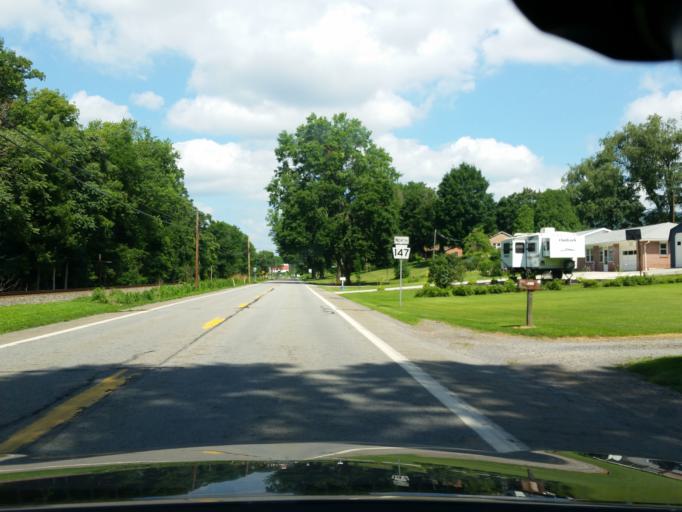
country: US
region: Pennsylvania
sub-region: Dauphin County
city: Millersburg
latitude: 40.4981
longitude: -76.9434
